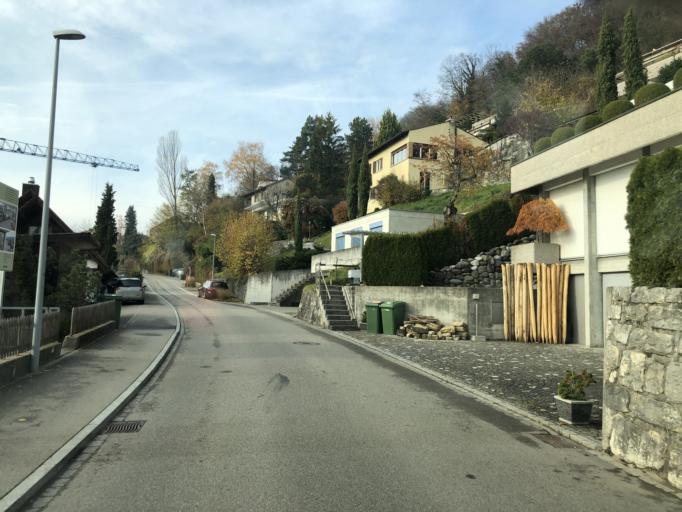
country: CH
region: Aargau
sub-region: Bezirk Baden
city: Wettingen
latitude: 47.4723
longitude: 8.3244
